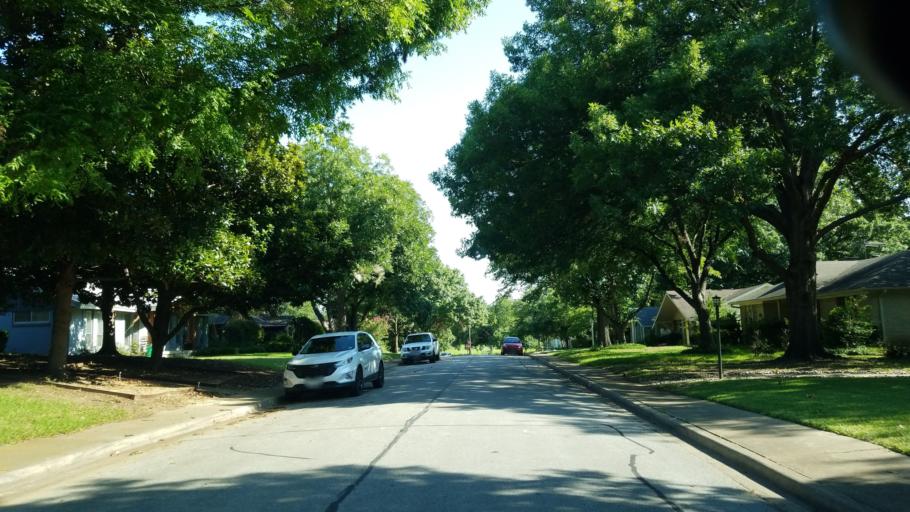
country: US
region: Texas
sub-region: Dallas County
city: Farmers Branch
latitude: 32.9279
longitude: -96.8865
